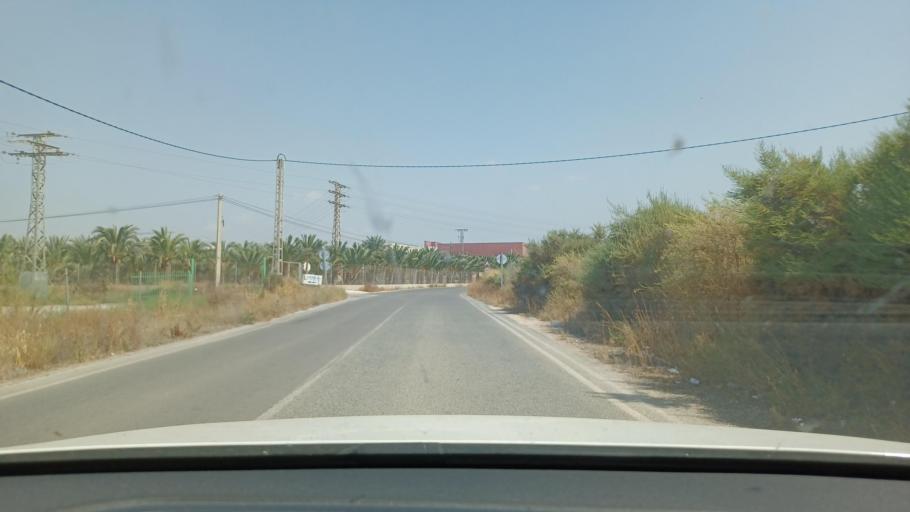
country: ES
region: Valencia
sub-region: Provincia de Alicante
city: Elche
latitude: 38.2483
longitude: -0.6913
